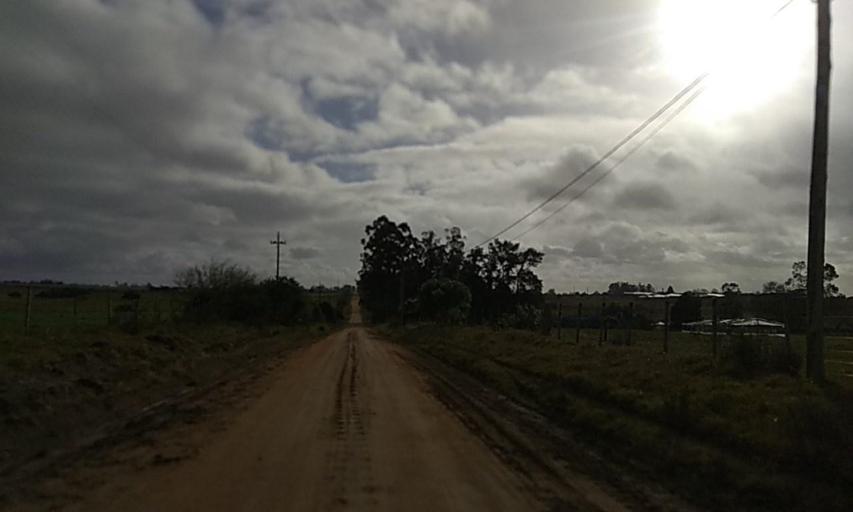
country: UY
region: Florida
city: Florida
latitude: -34.0619
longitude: -56.2296
